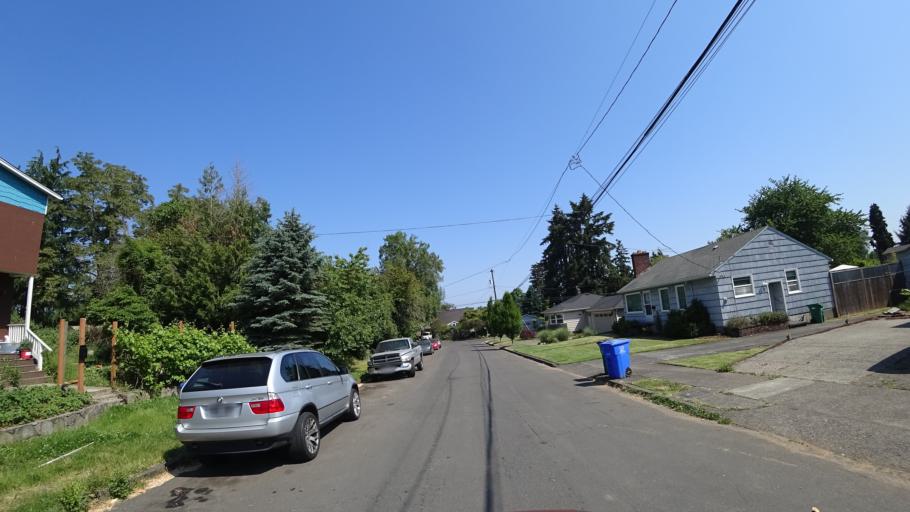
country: US
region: Oregon
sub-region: Multnomah County
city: Portland
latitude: 45.5678
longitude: -122.6461
